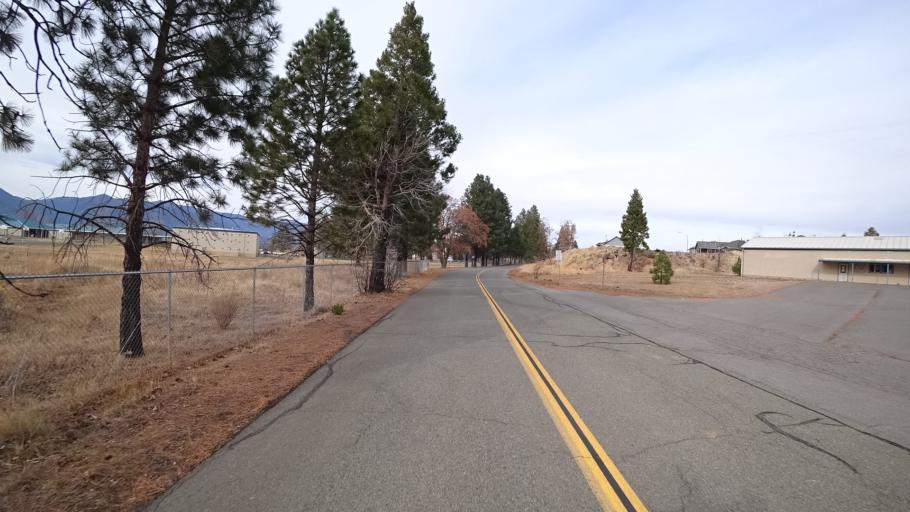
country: US
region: California
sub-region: Siskiyou County
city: Weed
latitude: 41.4285
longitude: -122.3787
